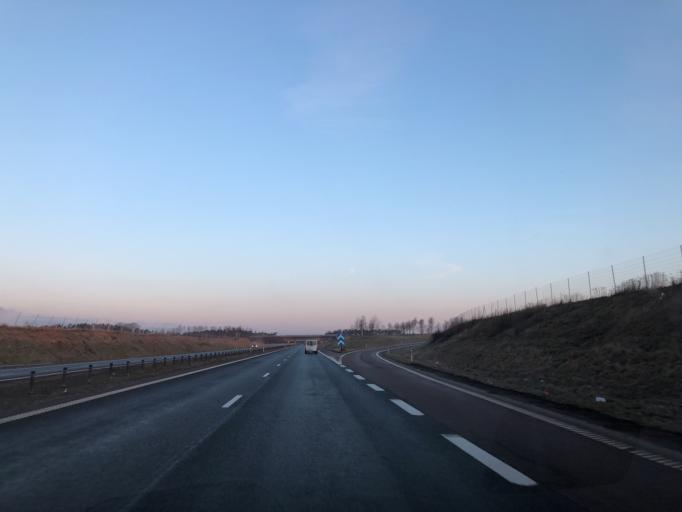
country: SE
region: Halland
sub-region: Laholms Kommun
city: Mellbystrand
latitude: 56.4491
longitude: 12.9515
